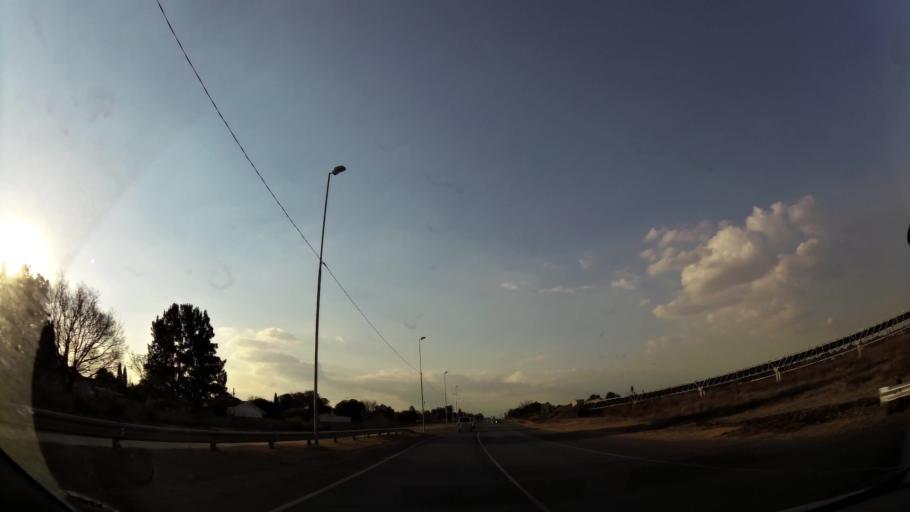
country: ZA
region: Gauteng
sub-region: Ekurhuleni Metropolitan Municipality
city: Boksburg
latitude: -26.2724
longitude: 28.2402
